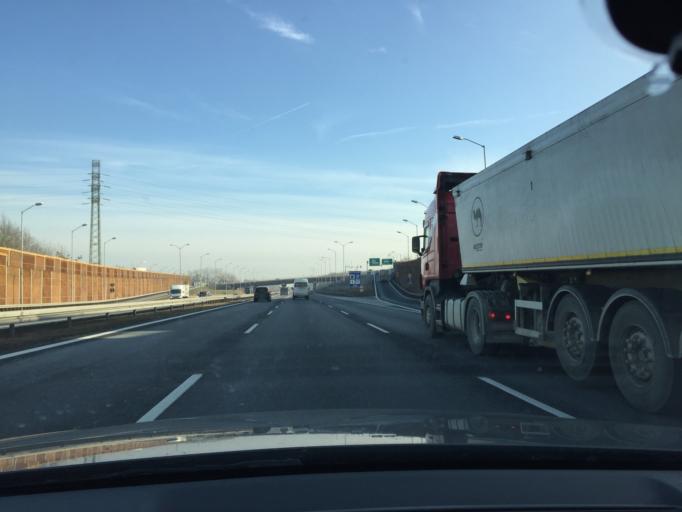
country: PL
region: Silesian Voivodeship
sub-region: Ruda Slaska
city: Ruda Slaska
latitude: 50.2564
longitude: 18.8503
